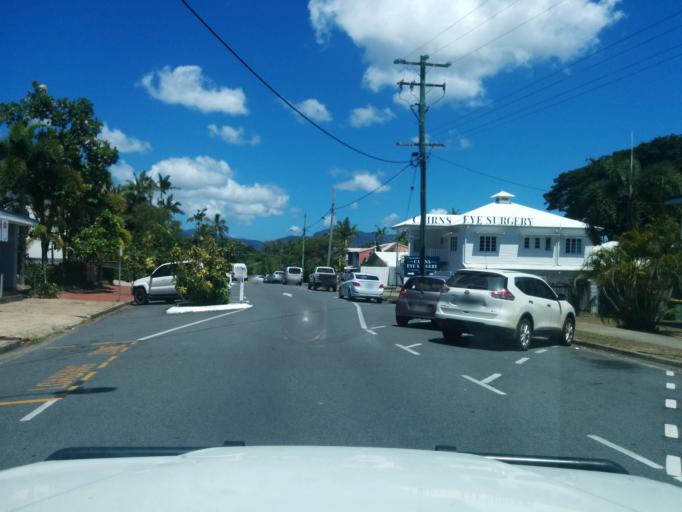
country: AU
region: Queensland
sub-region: Cairns
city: Cairns
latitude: -16.9013
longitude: 145.7424
